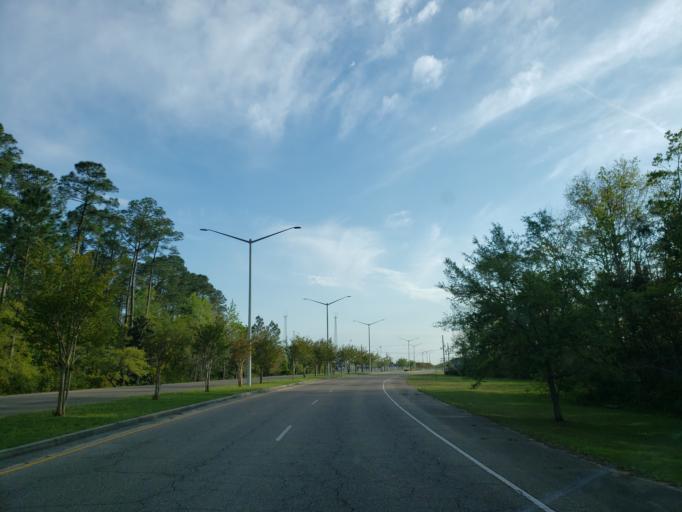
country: US
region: Mississippi
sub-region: Harrison County
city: West Gulfport
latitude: 30.4110
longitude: -89.0580
